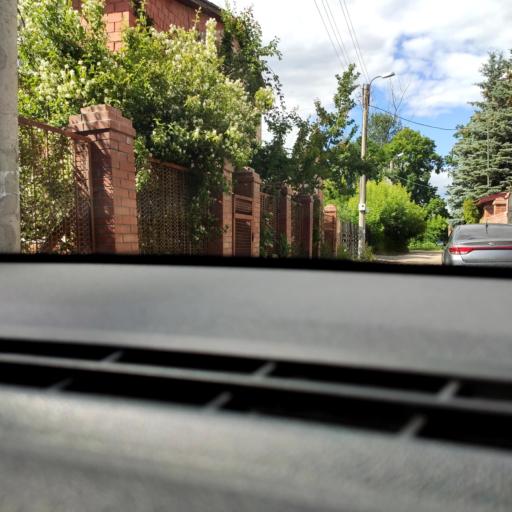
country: RU
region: Samara
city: Podstepki
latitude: 53.5846
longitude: 49.0692
